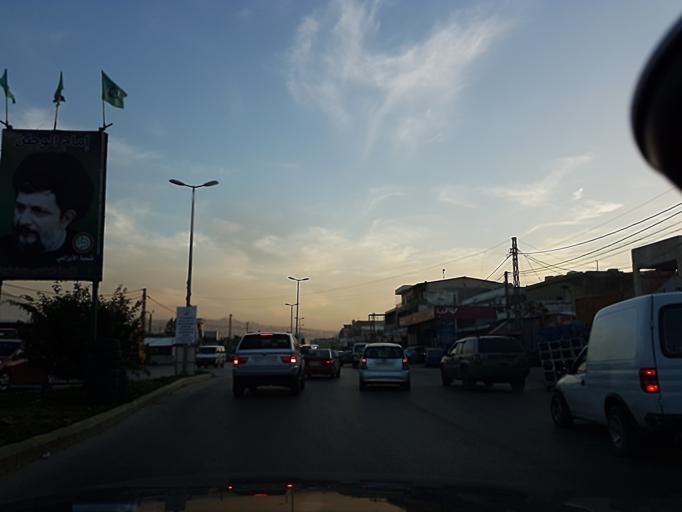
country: LB
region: Beyrouth
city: Beirut
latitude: 33.8315
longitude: 35.4843
